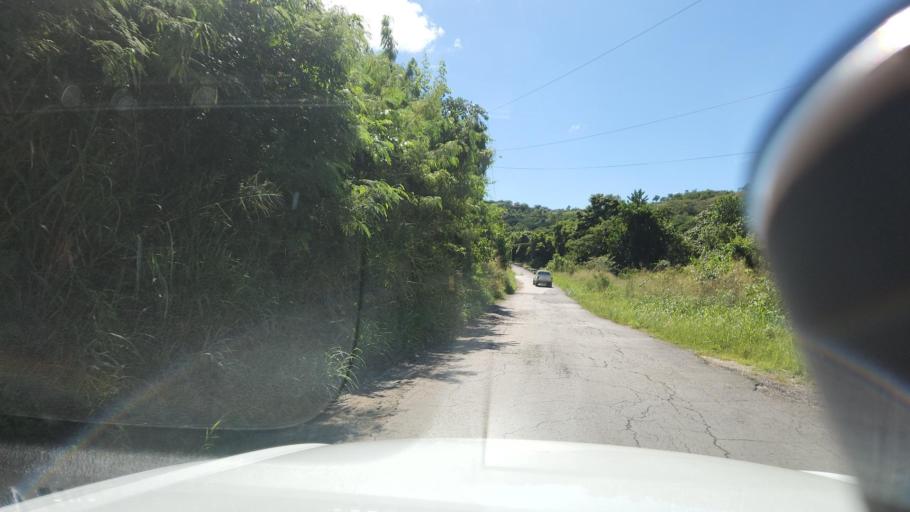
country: BB
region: Saint Andrew
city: Greenland
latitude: 13.2209
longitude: -59.5591
